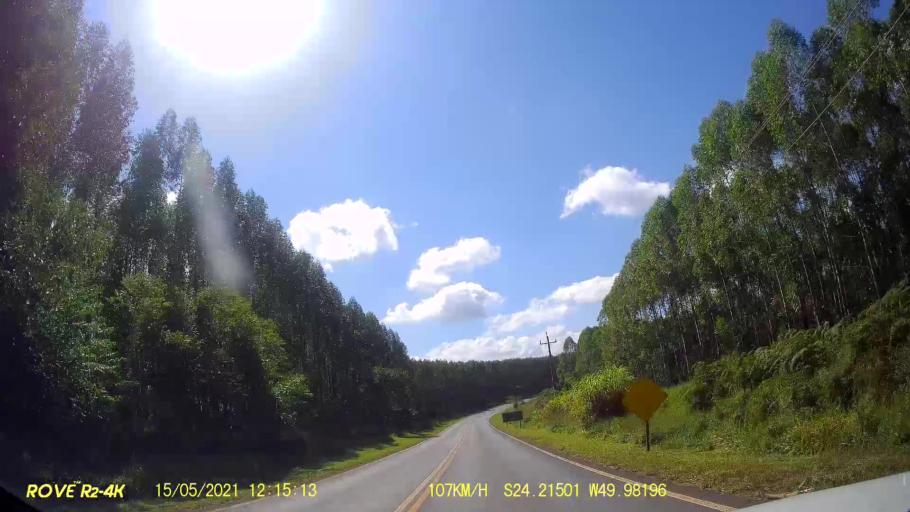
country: BR
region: Parana
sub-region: Jaguariaiva
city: Jaguariaiva
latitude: -24.2150
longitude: -49.9820
